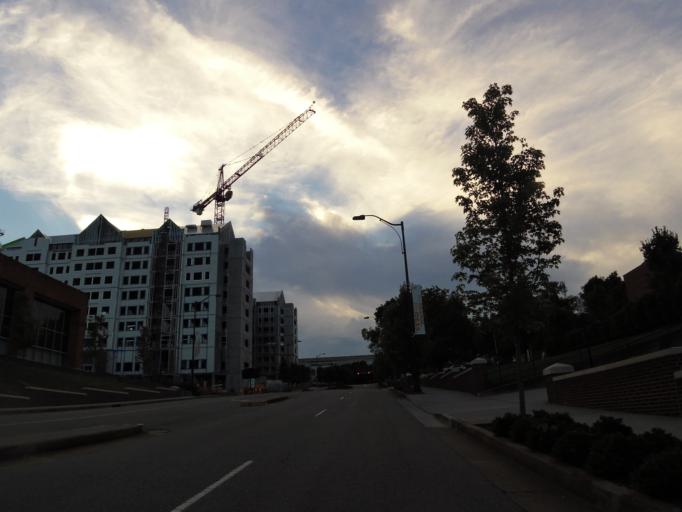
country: US
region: Tennessee
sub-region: Knox County
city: Knoxville
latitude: 35.9511
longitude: -83.9272
